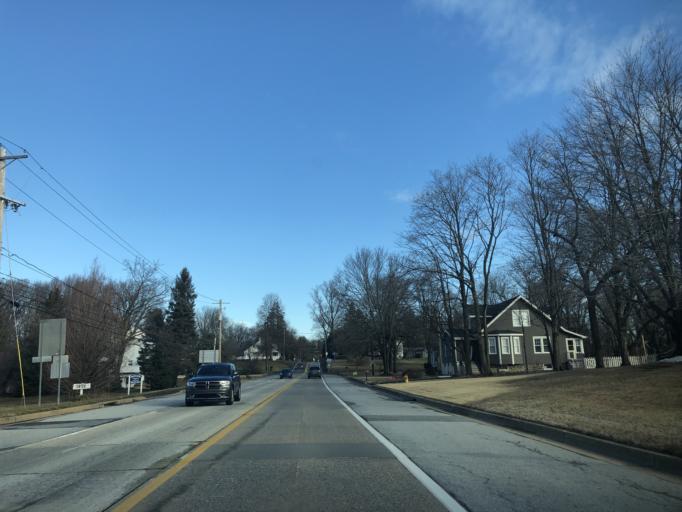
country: US
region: Delaware
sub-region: New Castle County
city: Claymont
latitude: 39.8319
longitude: -75.4993
